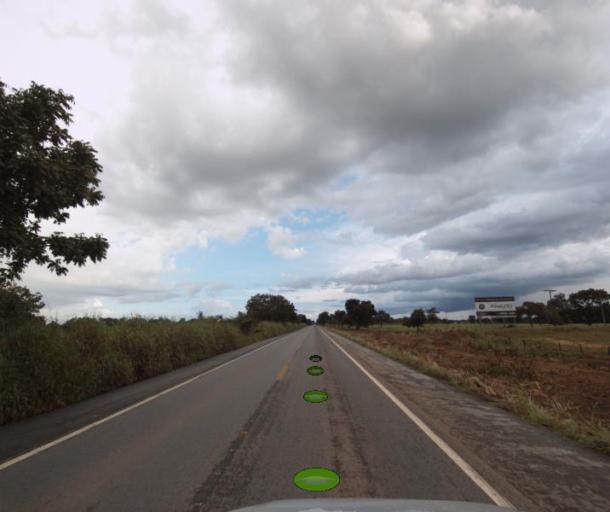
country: BR
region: Goias
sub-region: Porangatu
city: Porangatu
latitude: -13.3378
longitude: -49.1210
